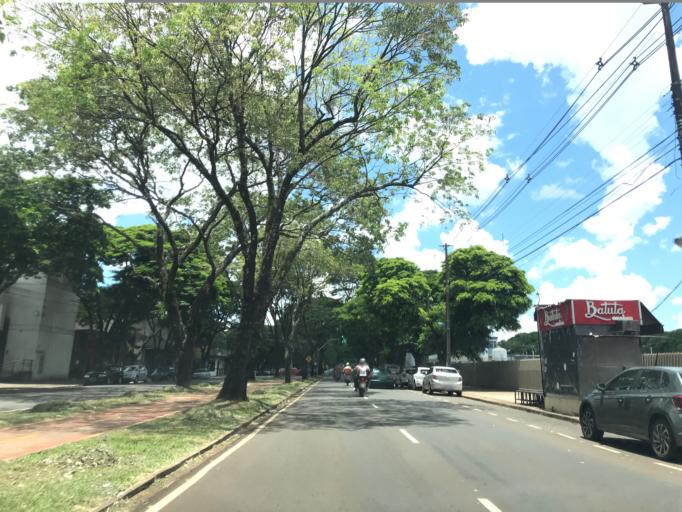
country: BR
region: Parana
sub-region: Maringa
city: Maringa
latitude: -23.4095
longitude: -51.9238
